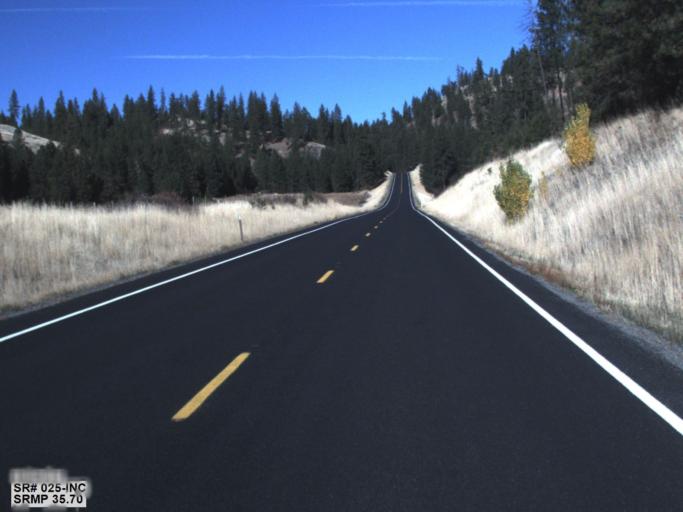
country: US
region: Washington
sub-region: Lincoln County
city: Davenport
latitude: 48.0442
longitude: -118.2240
